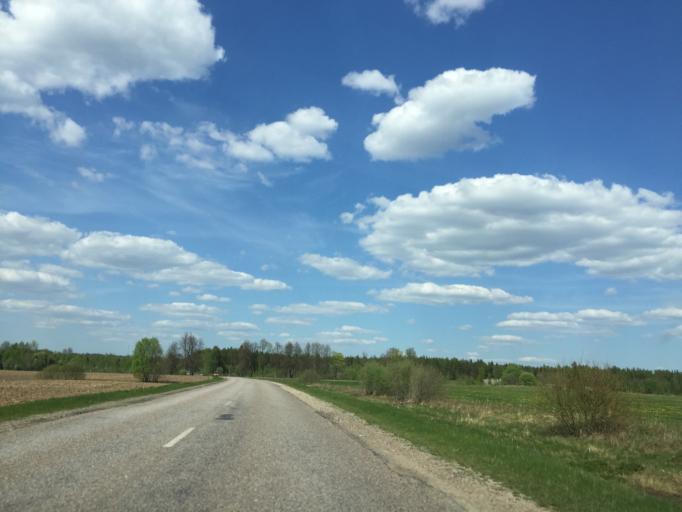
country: LV
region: Limbazu Rajons
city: Limbazi
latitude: 57.3864
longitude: 24.6883
